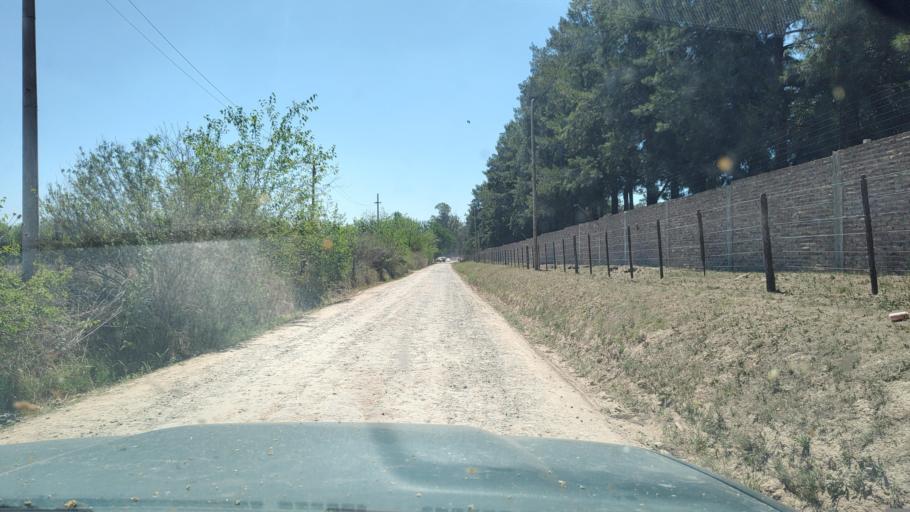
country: AR
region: Buenos Aires
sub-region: Partido de Lujan
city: Lujan
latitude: -34.5956
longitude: -59.1470
